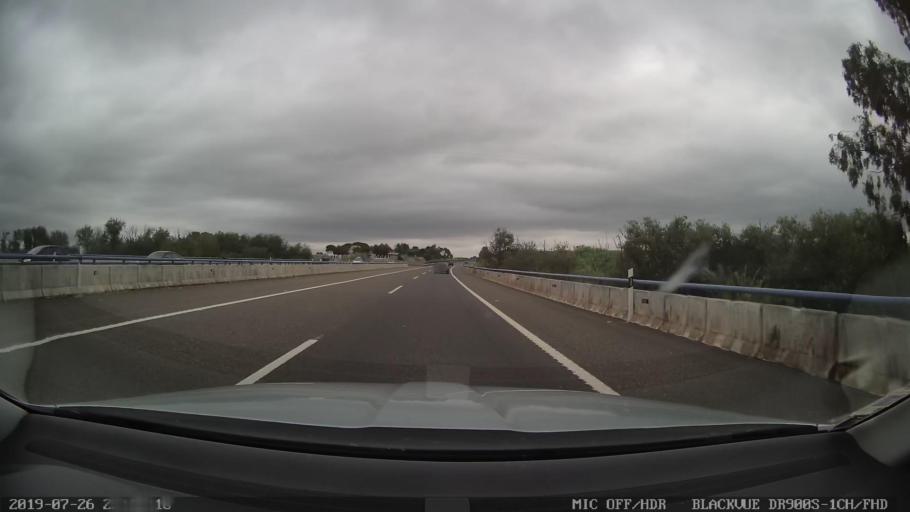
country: ES
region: Extremadura
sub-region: Provincia de Badajoz
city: Santa Amalia
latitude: 39.0935
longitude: -6.0156
